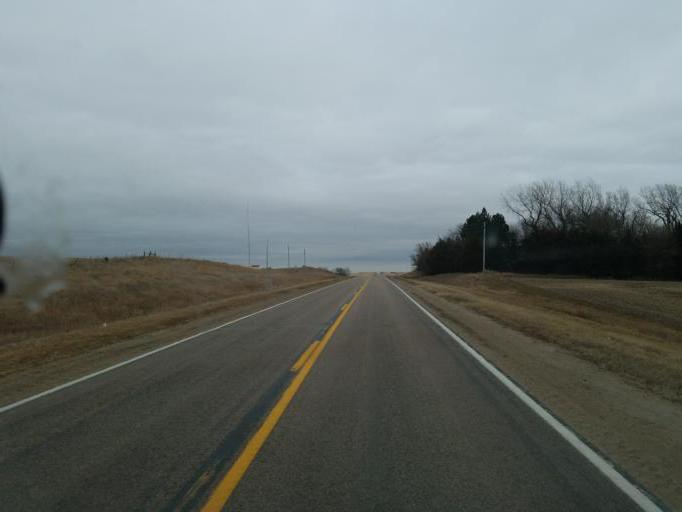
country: US
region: Nebraska
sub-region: Knox County
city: Bloomfield
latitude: 42.5979
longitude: -97.5709
